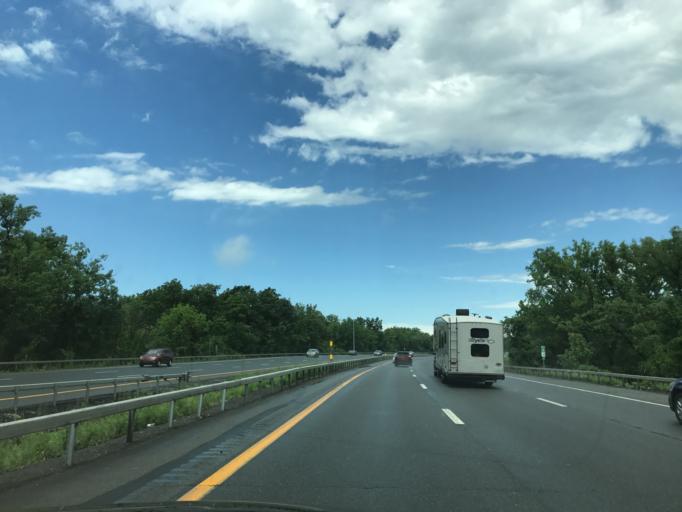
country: US
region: New York
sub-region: Albany County
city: Cohoes
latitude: 42.7928
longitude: -73.7624
